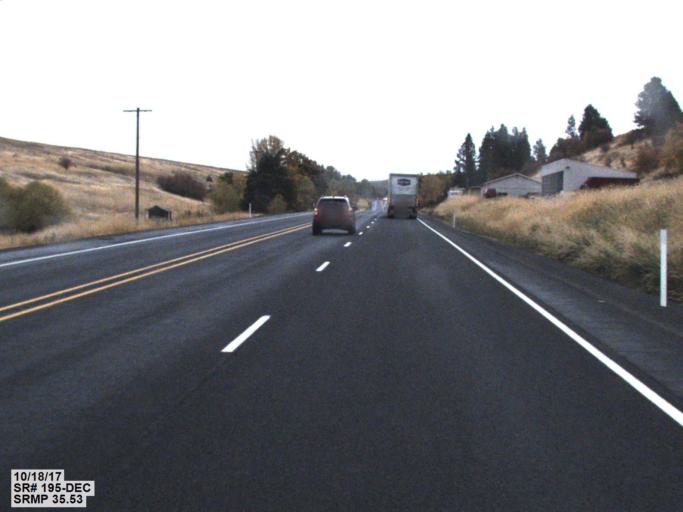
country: US
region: Washington
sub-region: Whitman County
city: Colfax
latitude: 46.8555
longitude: -117.3470
